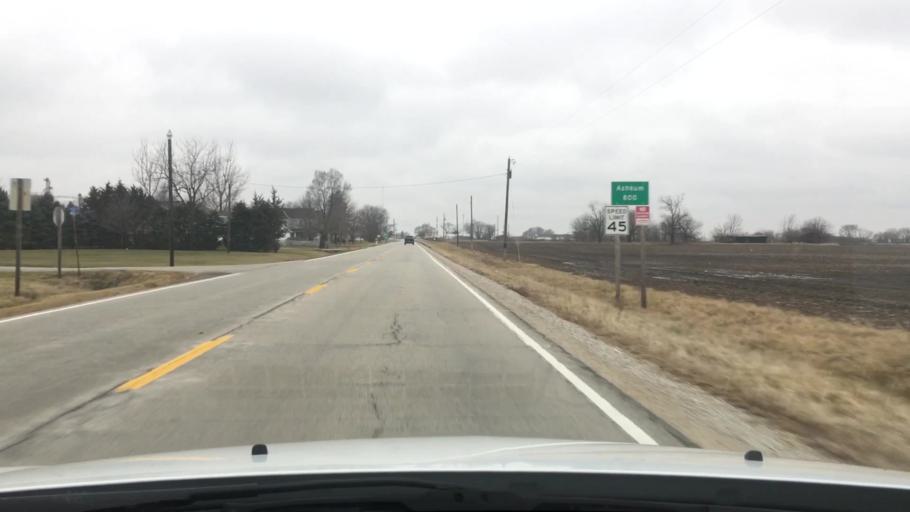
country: US
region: Illinois
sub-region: Iroquois County
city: Clifton
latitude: 40.8850
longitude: -87.9456
